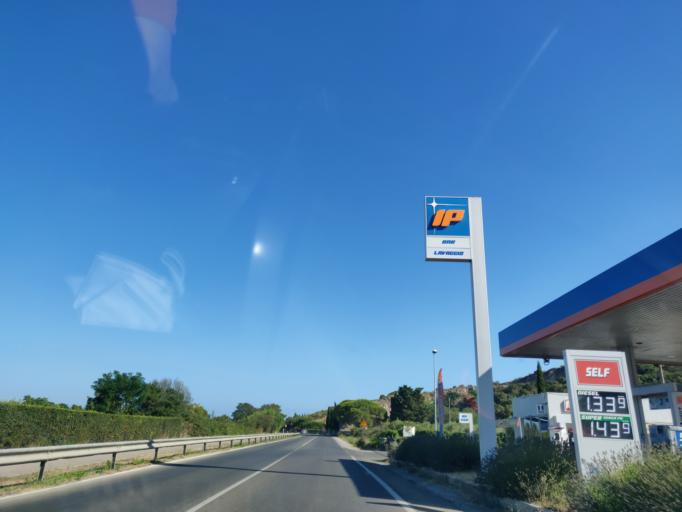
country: IT
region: Tuscany
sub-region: Provincia di Grosseto
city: Porto Ercole
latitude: 42.4258
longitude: 11.1977
